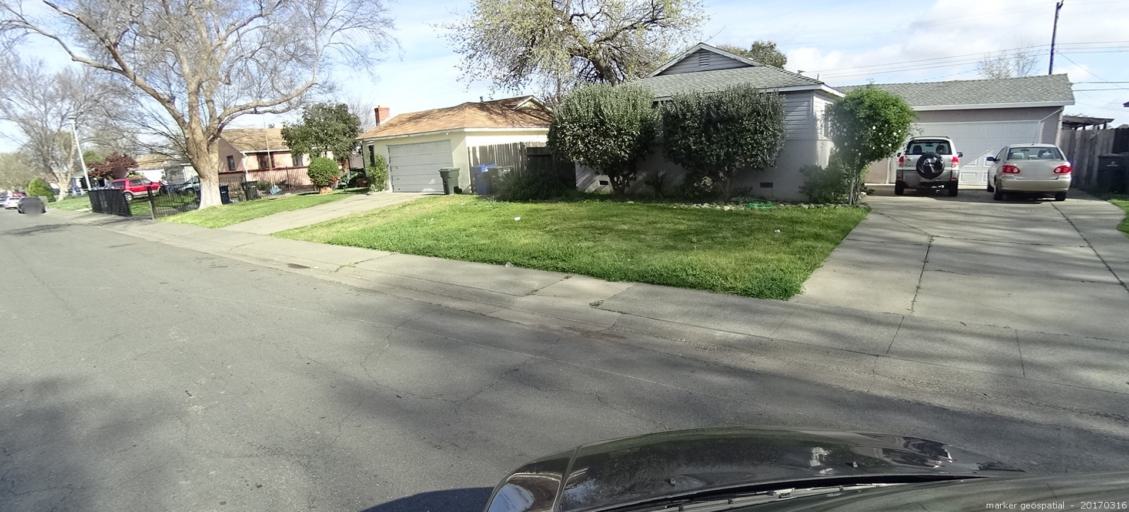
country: US
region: California
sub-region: Sacramento County
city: Parkway
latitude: 38.5111
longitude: -121.4898
